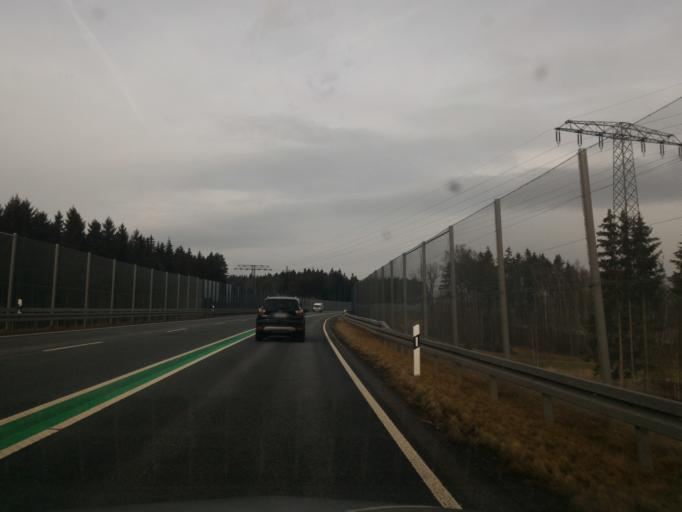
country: DE
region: Saxony
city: Eibau
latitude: 51.0027
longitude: 14.6849
